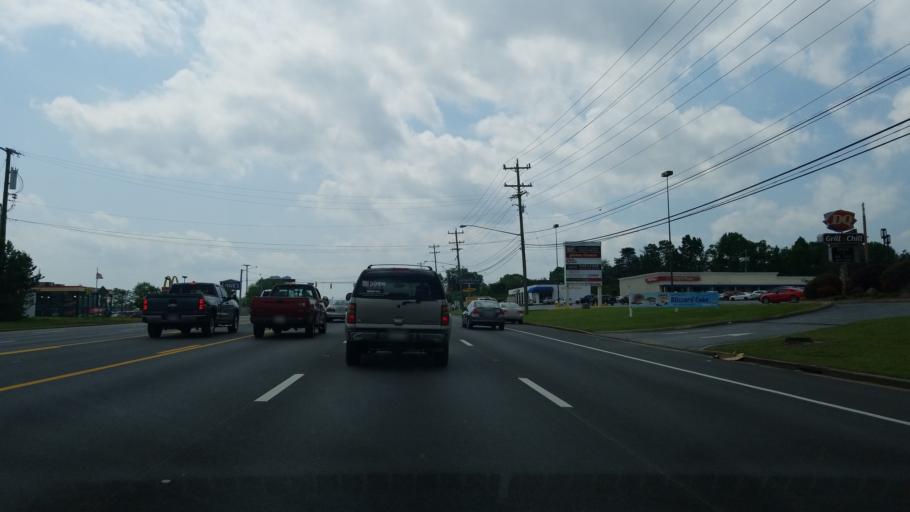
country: US
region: Tennessee
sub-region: Hamilton County
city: Red Bank
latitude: 35.1397
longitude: -85.2483
